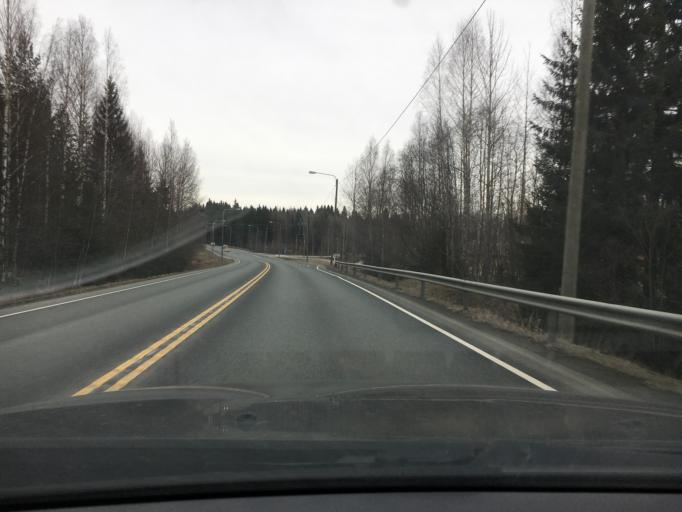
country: FI
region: Northern Savo
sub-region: Kuopio
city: Siilinjaervi
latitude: 63.0920
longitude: 27.6521
